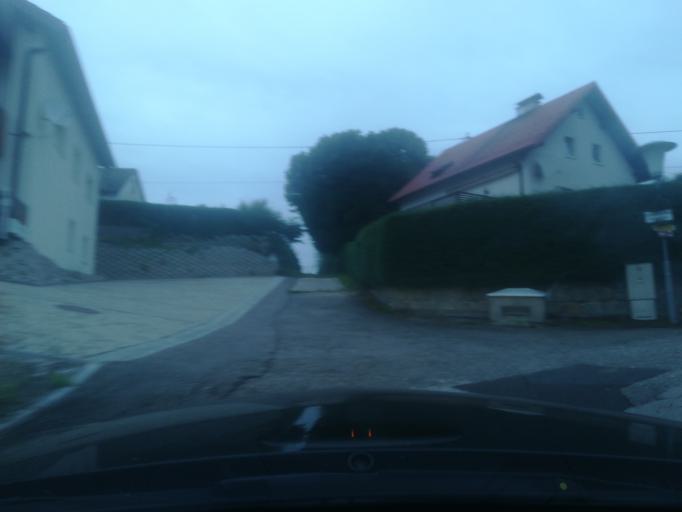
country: AT
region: Upper Austria
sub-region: Politischer Bezirk Urfahr-Umgebung
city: Engerwitzdorf
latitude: 48.3611
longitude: 14.5209
